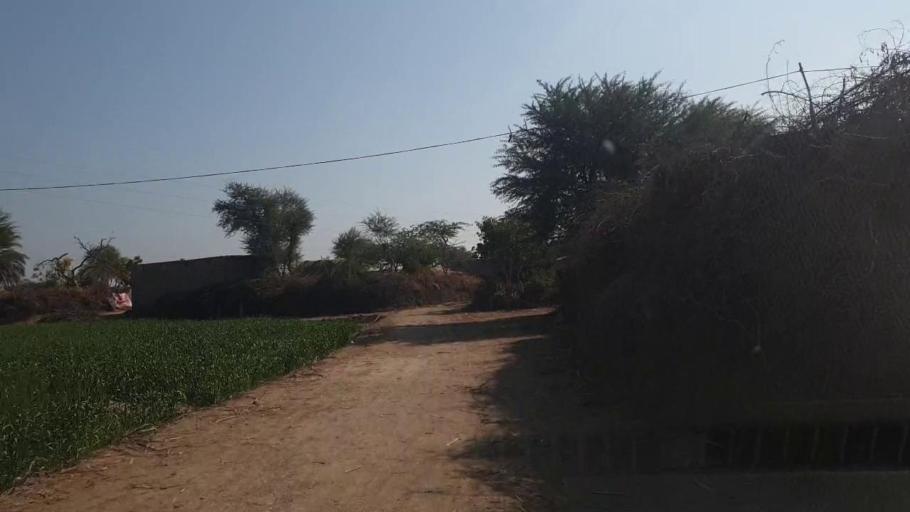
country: PK
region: Sindh
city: Shahdadpur
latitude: 26.0447
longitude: 68.4566
